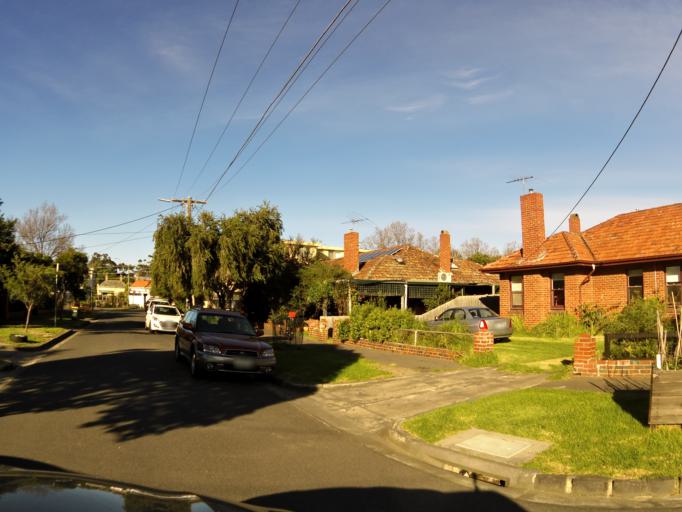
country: AU
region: Victoria
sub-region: Yarra
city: Richmond
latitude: -37.8232
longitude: 145.0112
